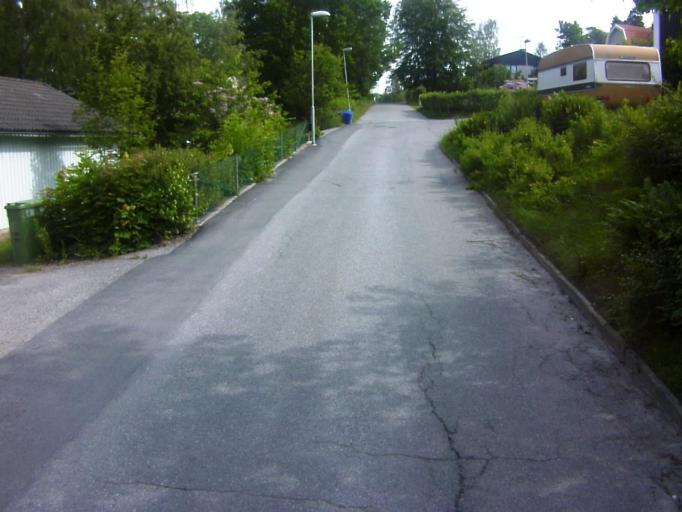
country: SE
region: Soedermanland
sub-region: Eskilstuna Kommun
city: Skogstorp
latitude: 59.3300
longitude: 16.4813
